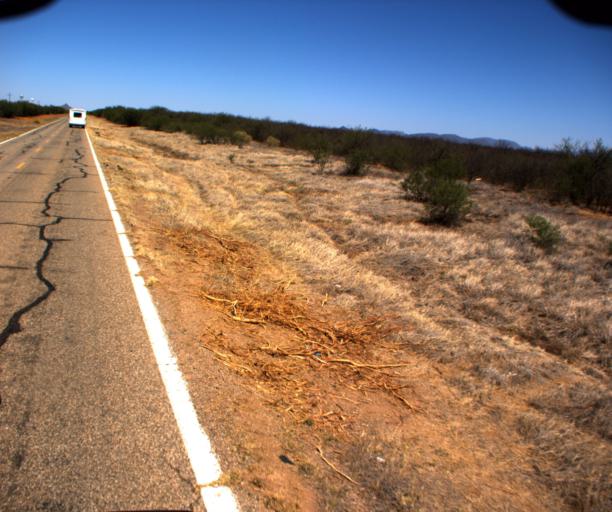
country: US
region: Arizona
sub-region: Pima County
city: Ajo
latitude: 32.1859
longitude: -112.3748
